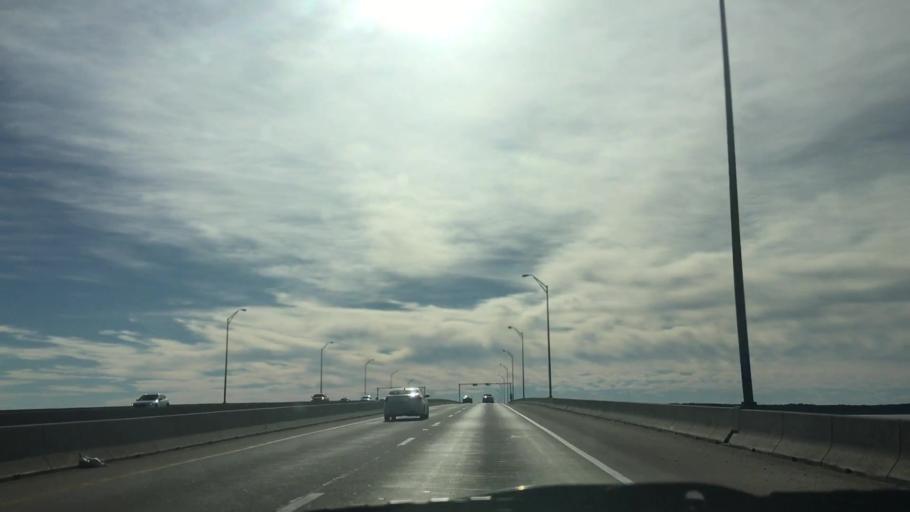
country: US
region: Virginia
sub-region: City of Newport News
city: Newport News
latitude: 36.9114
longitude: -76.4078
